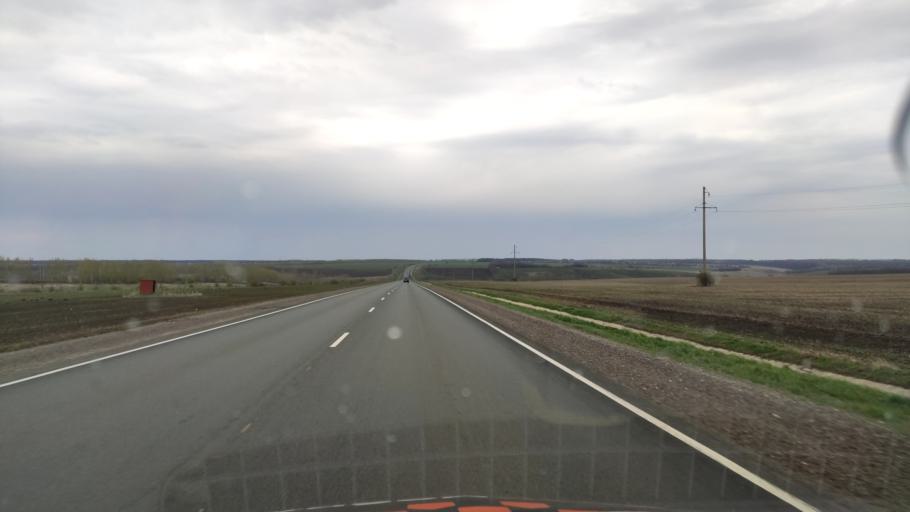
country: RU
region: Voronezj
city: Latnaya
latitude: 51.6449
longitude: 38.7123
